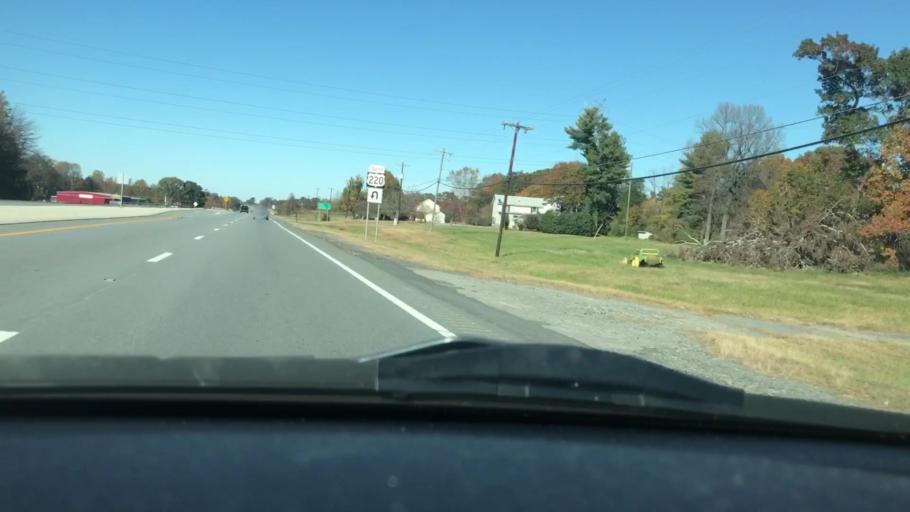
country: US
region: North Carolina
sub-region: Guilford County
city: Stokesdale
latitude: 36.2954
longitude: -79.9402
